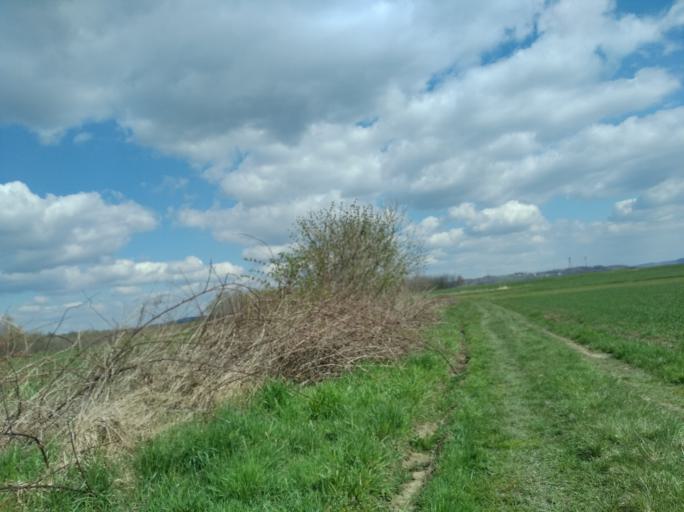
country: PL
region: Subcarpathian Voivodeship
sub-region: Powiat strzyzowski
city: Strzyzow
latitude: 49.8473
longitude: 21.7892
